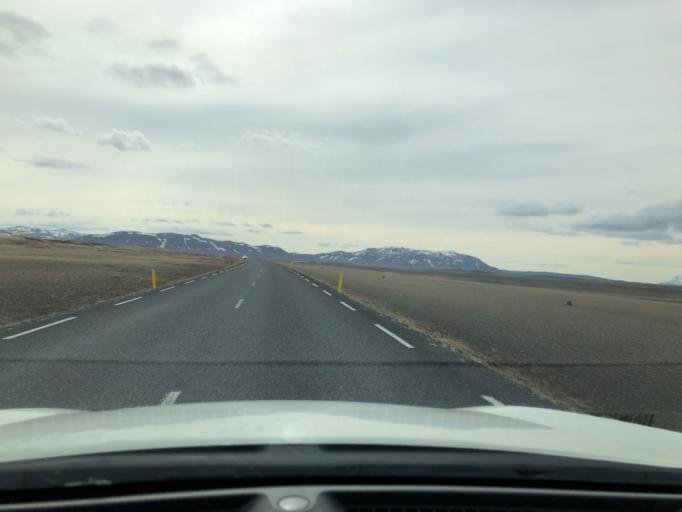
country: IS
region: Northeast
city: Laugar
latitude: 65.6127
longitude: -16.1587
